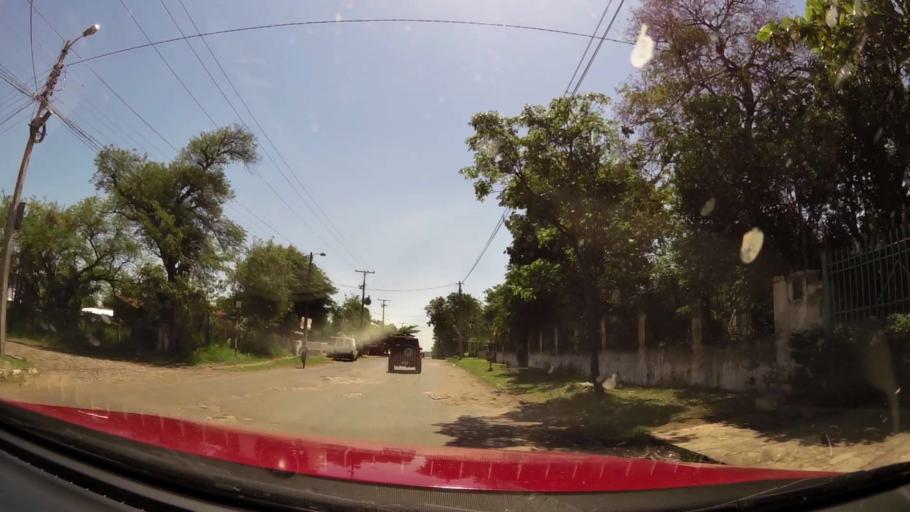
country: PY
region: Central
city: Colonia Mariano Roque Alonso
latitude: -25.2268
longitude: -57.5545
